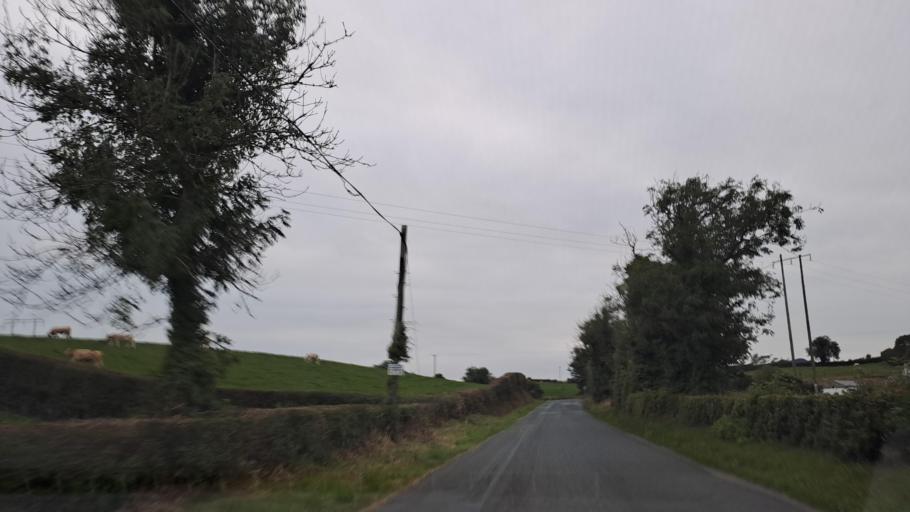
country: IE
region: Ulster
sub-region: County Monaghan
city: Carrickmacross
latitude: 54.0217
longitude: -6.7774
